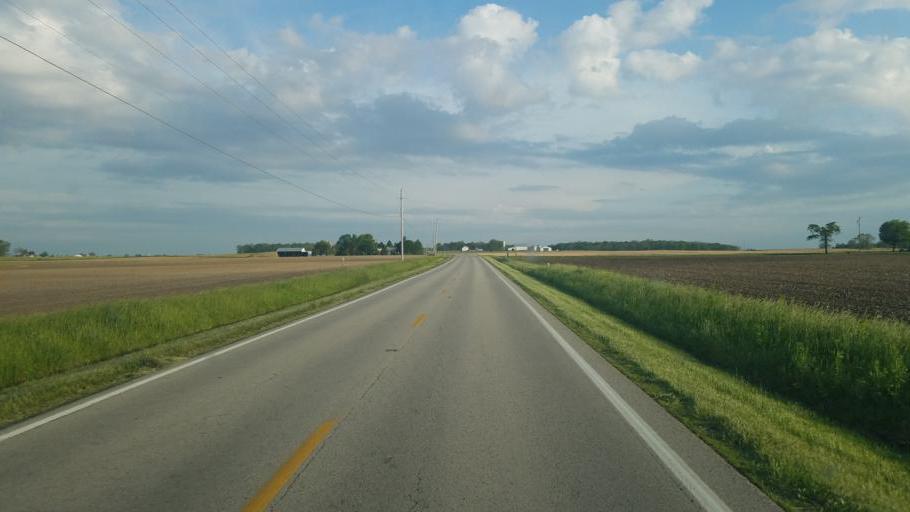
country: US
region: Ohio
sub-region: Clinton County
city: Sabina
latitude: 39.4464
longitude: -83.6434
